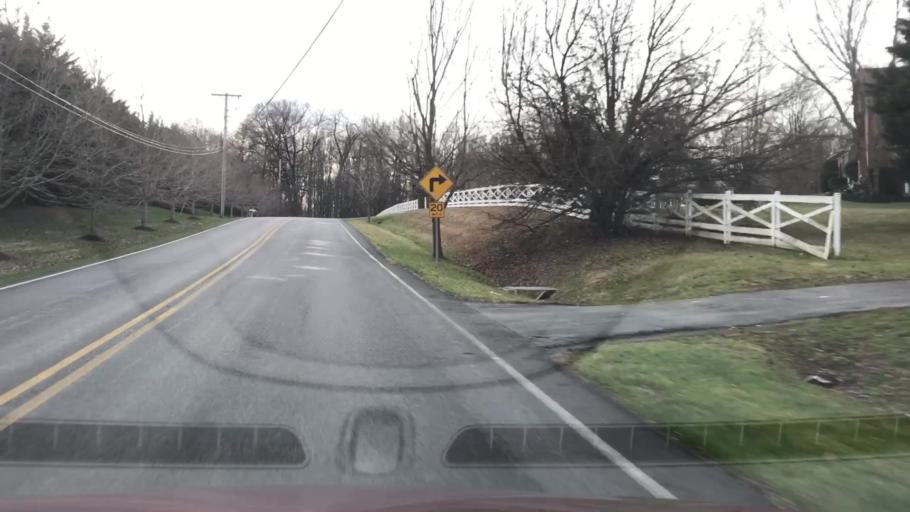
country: US
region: Maryland
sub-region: Howard County
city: Fulton
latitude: 39.1689
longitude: -76.9212
